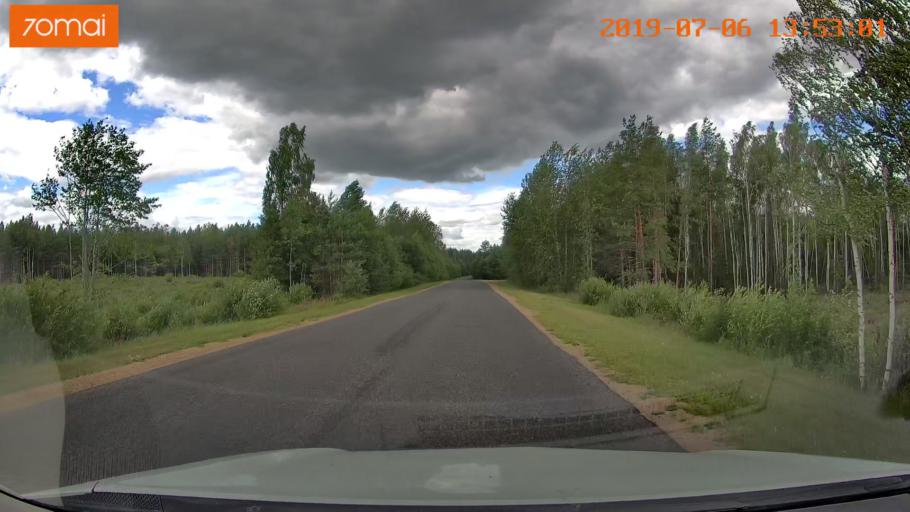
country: BY
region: Minsk
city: Ivyanyets
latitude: 53.7283
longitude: 26.8266
